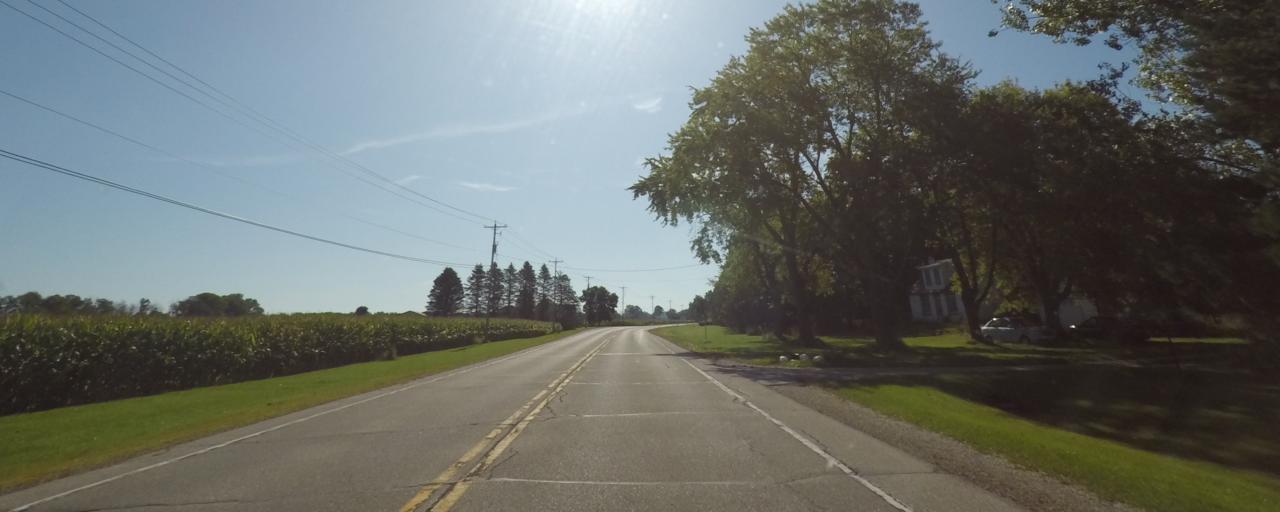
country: US
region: Wisconsin
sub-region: Waukesha County
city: Dousman
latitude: 43.0270
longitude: -88.5070
